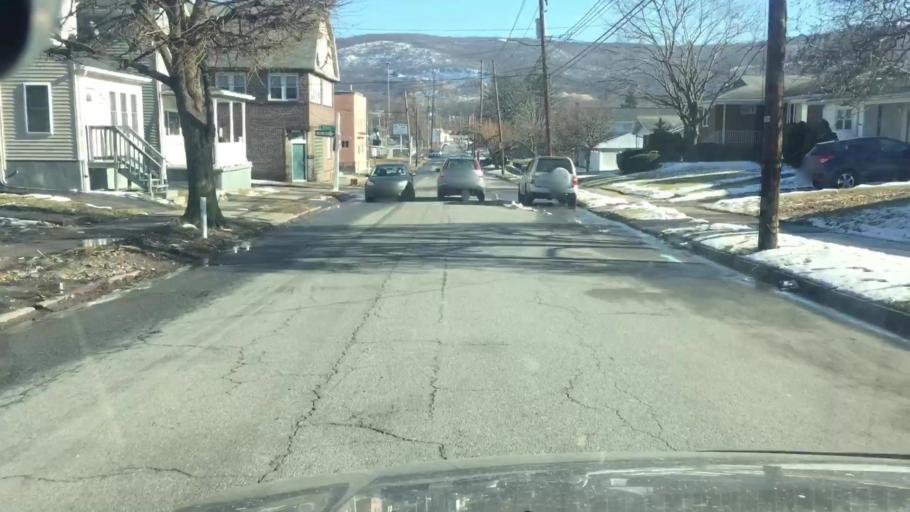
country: US
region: Pennsylvania
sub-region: Luzerne County
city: Wilkes-Barre
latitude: 41.2300
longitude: -75.8895
